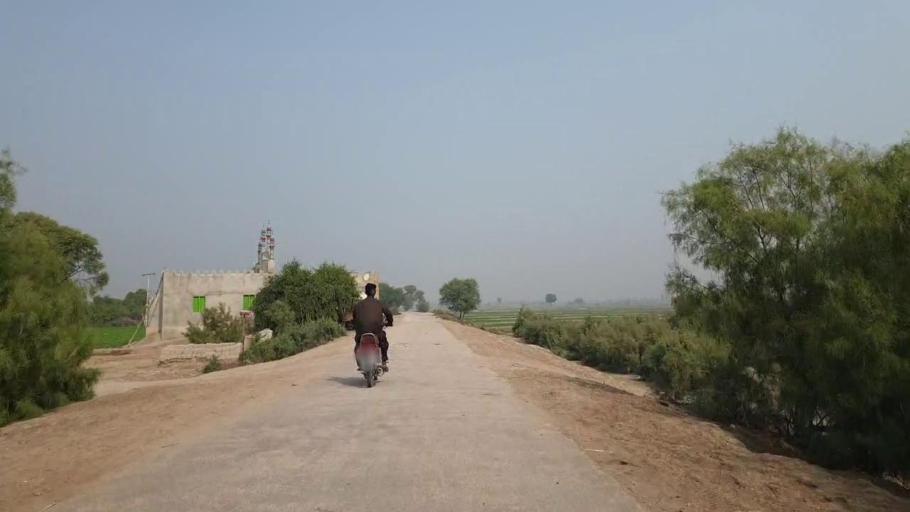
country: PK
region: Sindh
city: Bhan
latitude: 26.5237
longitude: 67.6914
